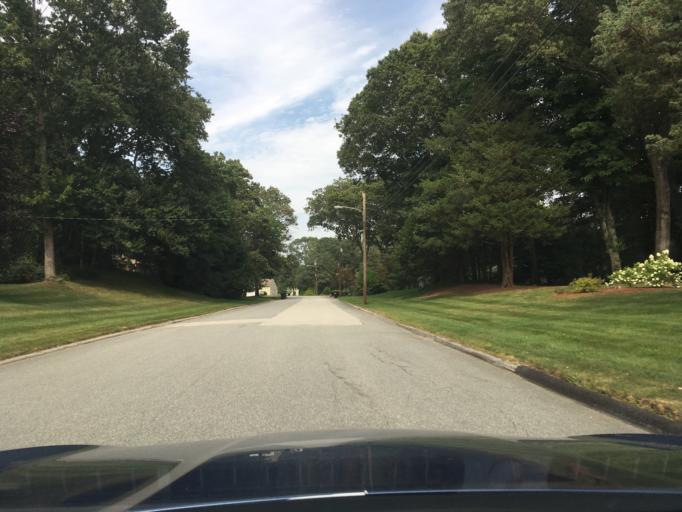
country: US
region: Rhode Island
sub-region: Kent County
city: East Greenwich
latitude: 41.6543
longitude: -71.4686
